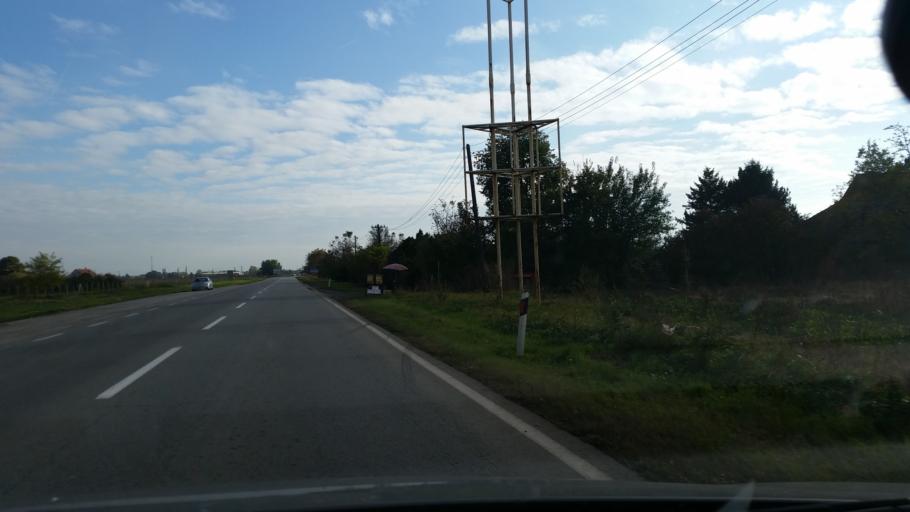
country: RS
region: Autonomna Pokrajina Vojvodina
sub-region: Srednjebanatski Okrug
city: Zrenjanin
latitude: 45.4085
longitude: 20.3744
